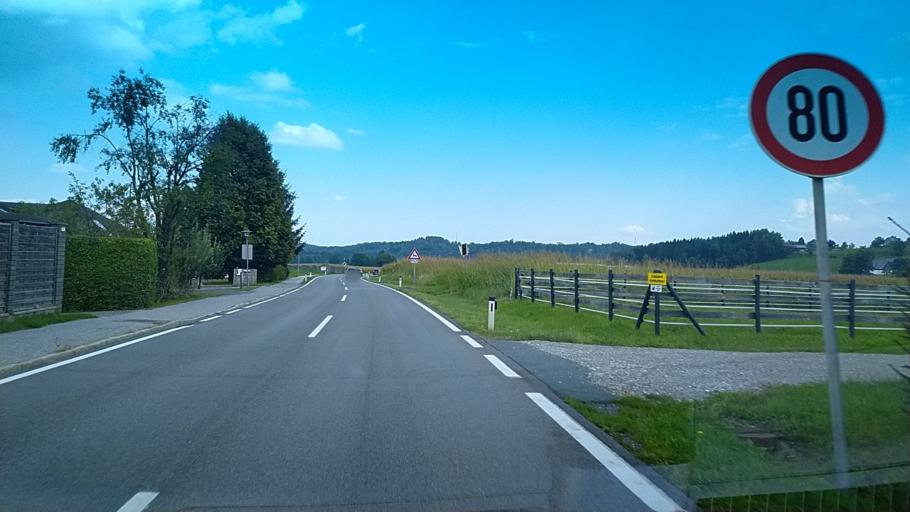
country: AT
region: Styria
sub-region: Politischer Bezirk Deutschlandsberg
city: Schwanberg
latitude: 46.7549
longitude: 15.2117
